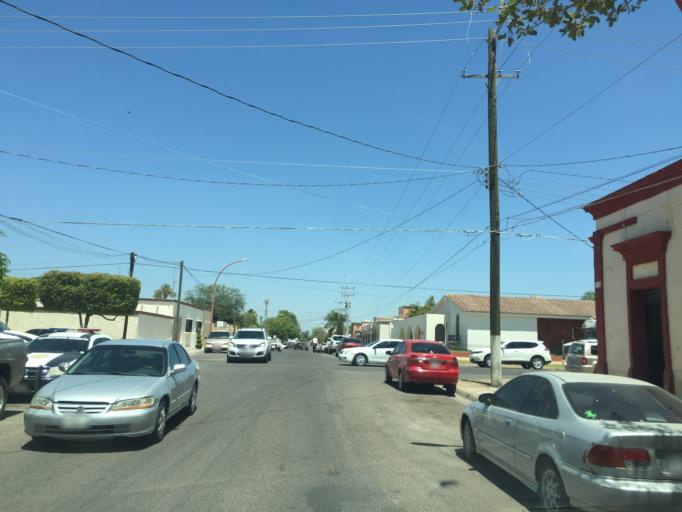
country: MX
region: Sonora
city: Navojoa
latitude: 27.0834
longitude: -109.4480
